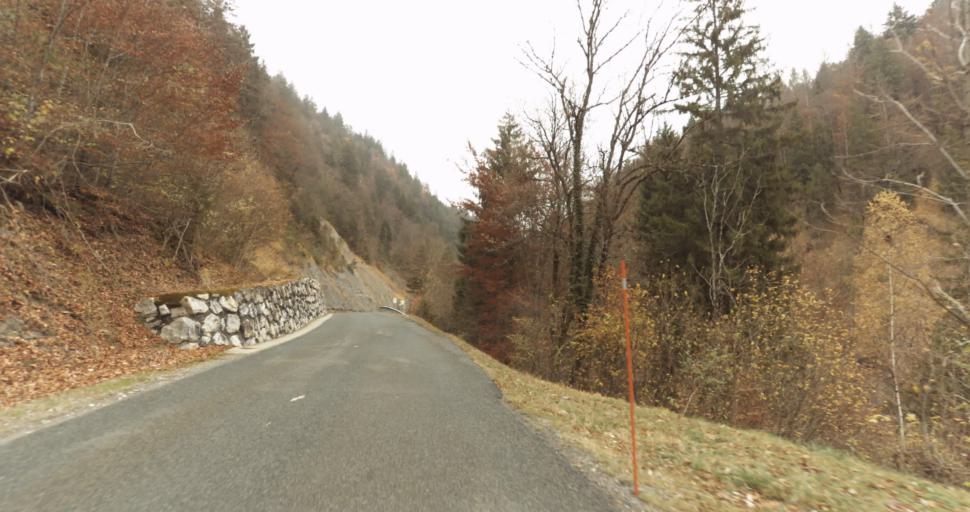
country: FR
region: Rhone-Alpes
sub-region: Departement de la Haute-Savoie
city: Doussard
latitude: 45.7878
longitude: 6.2586
